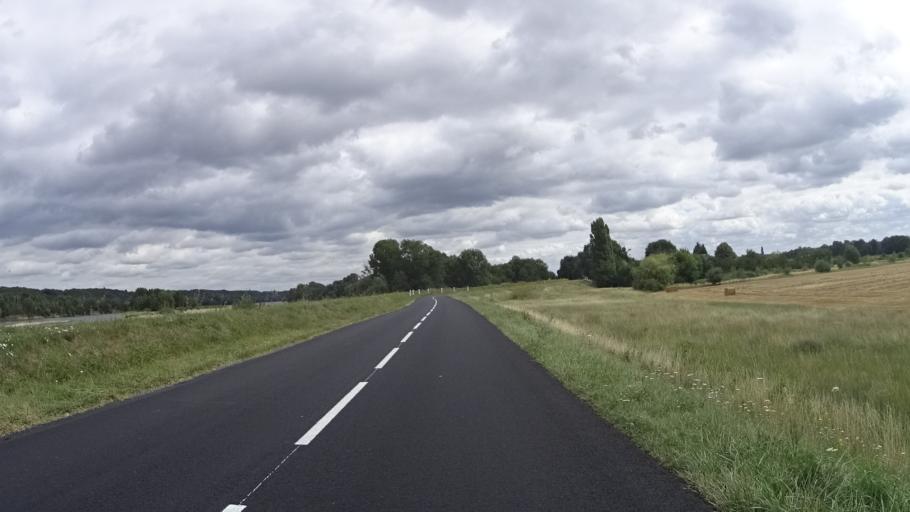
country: FR
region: Centre
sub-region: Departement d'Indre-et-Loire
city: Cheille
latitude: 47.2788
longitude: 0.3257
